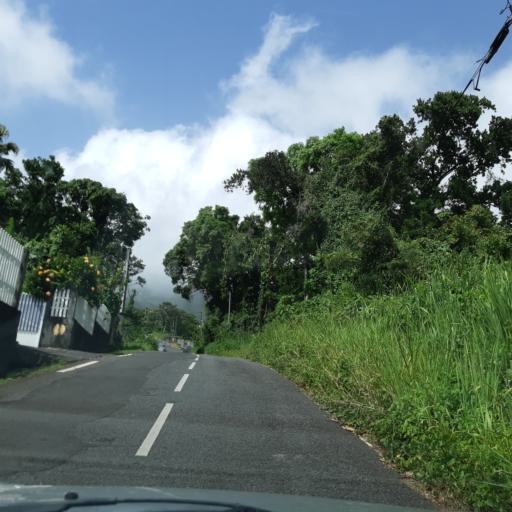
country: GP
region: Guadeloupe
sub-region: Guadeloupe
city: Saint-Claude
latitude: 16.0299
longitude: -61.6888
